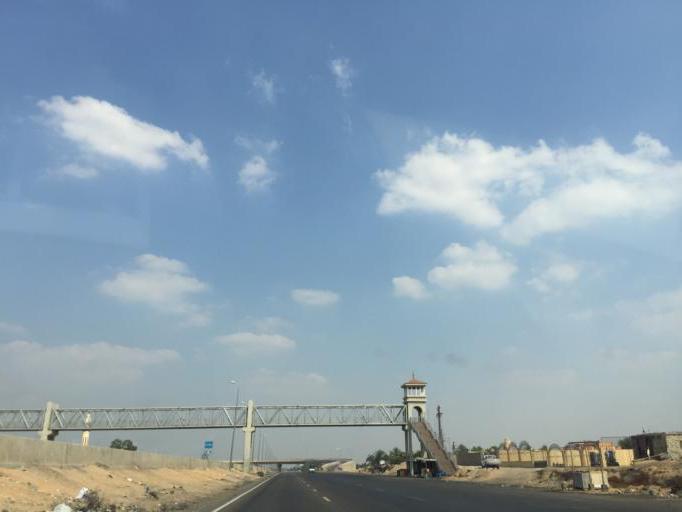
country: EG
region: Al Buhayrah
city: Beheira
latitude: 30.3181
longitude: 30.5396
